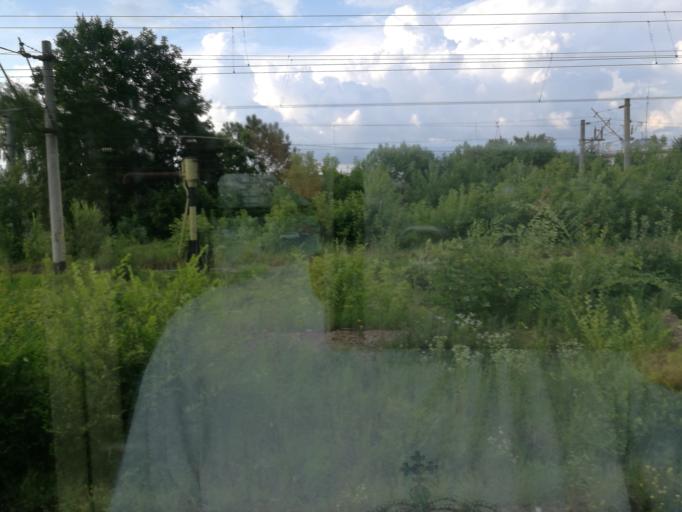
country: RO
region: Brasov
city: Brasov
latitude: 45.6610
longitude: 25.6200
